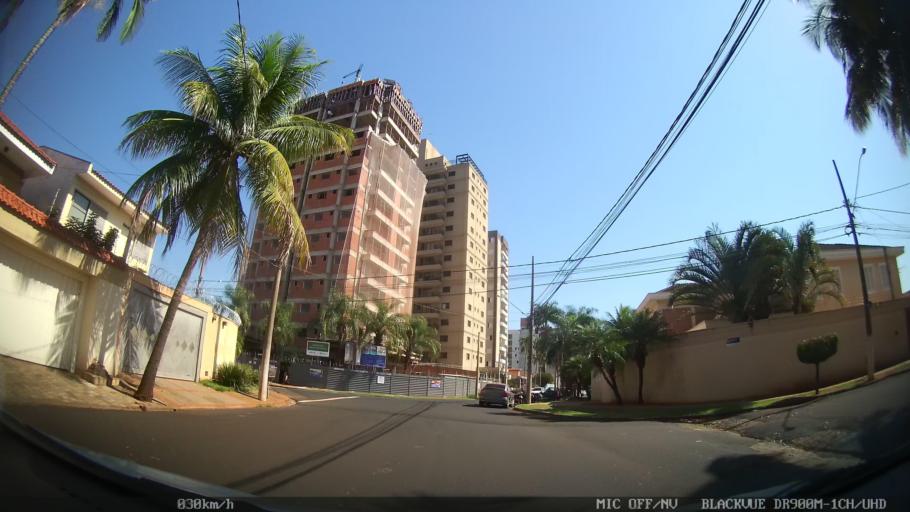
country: BR
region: Sao Paulo
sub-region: Ribeirao Preto
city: Ribeirao Preto
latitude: -21.2016
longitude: -47.7743
